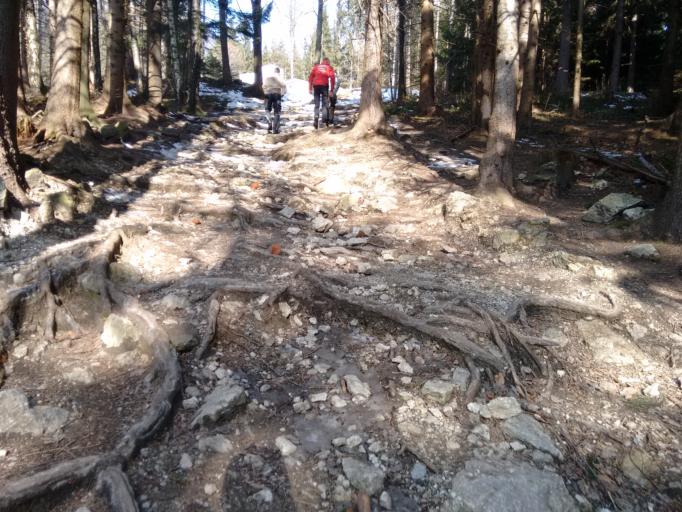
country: AT
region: Styria
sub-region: Politischer Bezirk Graz-Umgebung
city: Sankt Radegund bei Graz
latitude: 47.1875
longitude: 15.4846
